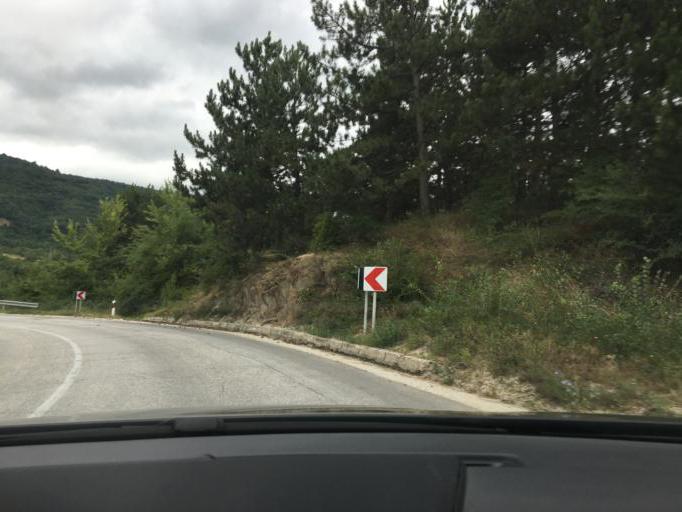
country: MK
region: Kriva Palanka
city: Kriva Palanka
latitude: 42.1847
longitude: 22.2790
